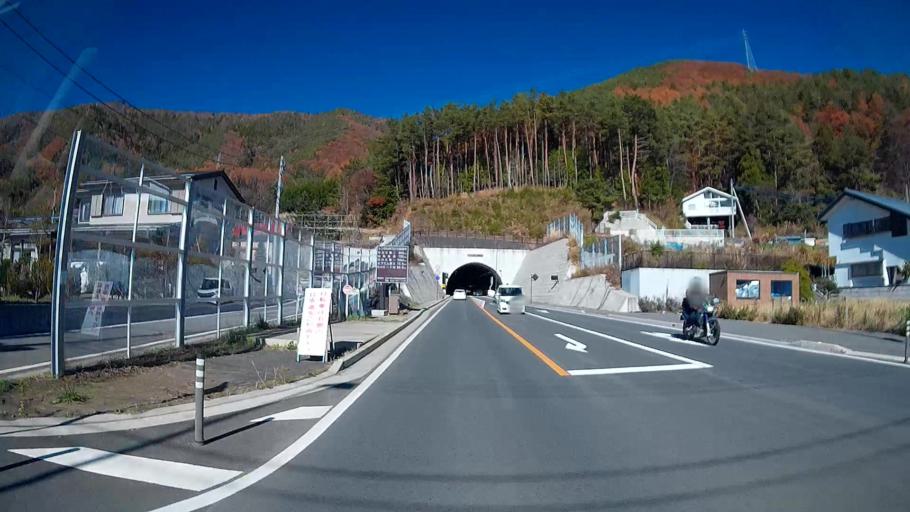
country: JP
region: Yamanashi
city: Fujikawaguchiko
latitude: 35.4993
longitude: 138.7911
